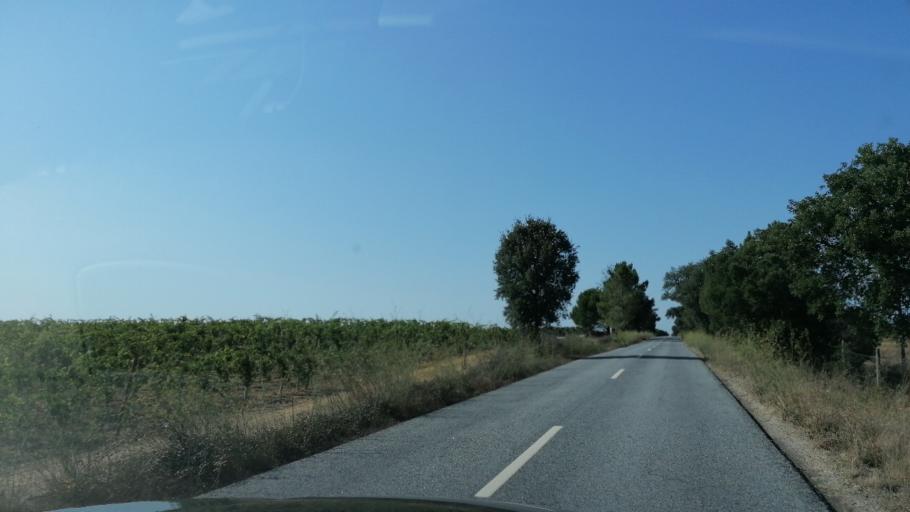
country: PT
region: Evora
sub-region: Vendas Novas
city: Vendas Novas
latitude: 38.7394
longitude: -8.6268
